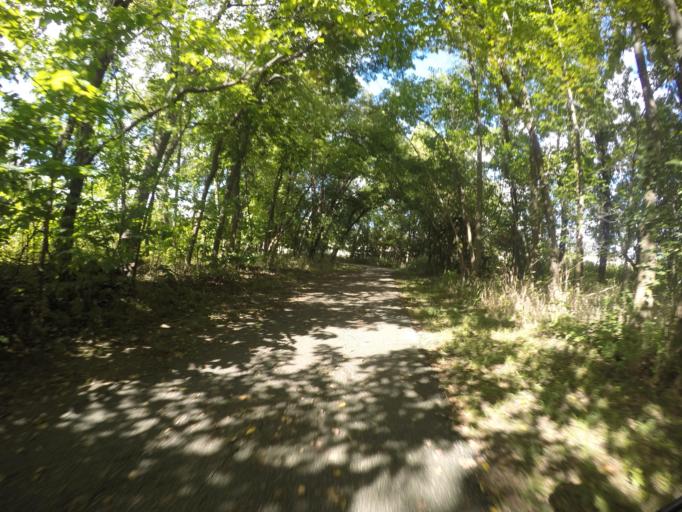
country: US
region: Kansas
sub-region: Johnson County
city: Lenexa
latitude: 38.9338
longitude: -94.6929
